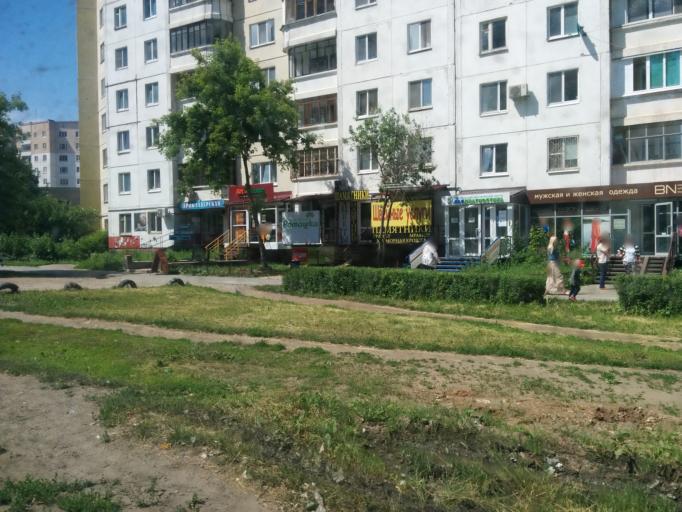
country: RU
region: Perm
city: Perm
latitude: 58.0029
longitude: 56.3046
